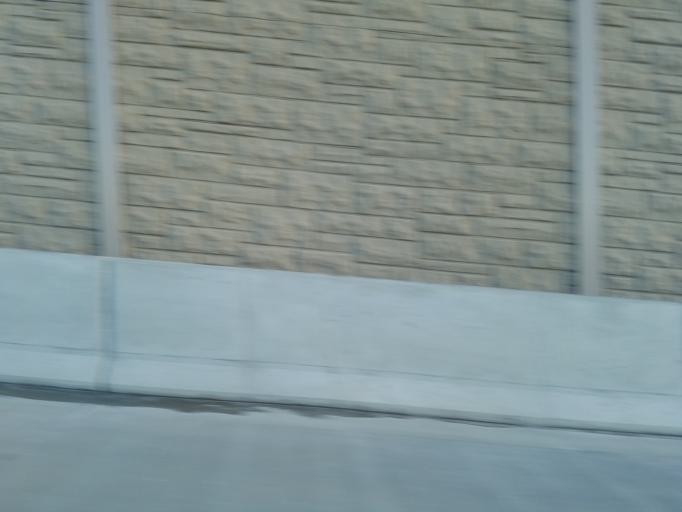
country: US
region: Illinois
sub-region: DuPage County
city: Itasca
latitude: 41.9818
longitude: -88.0195
